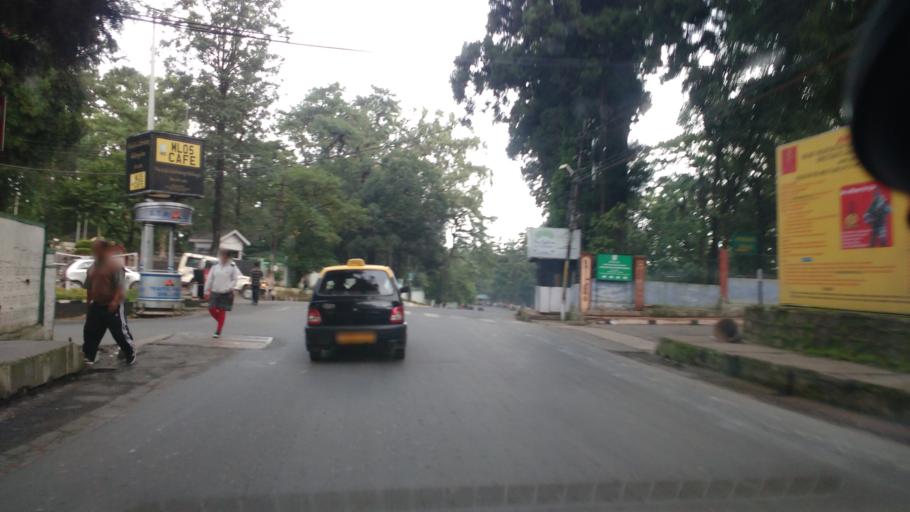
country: IN
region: Meghalaya
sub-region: East Khasi Hills
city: Shillong
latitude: 25.5696
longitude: 91.8785
